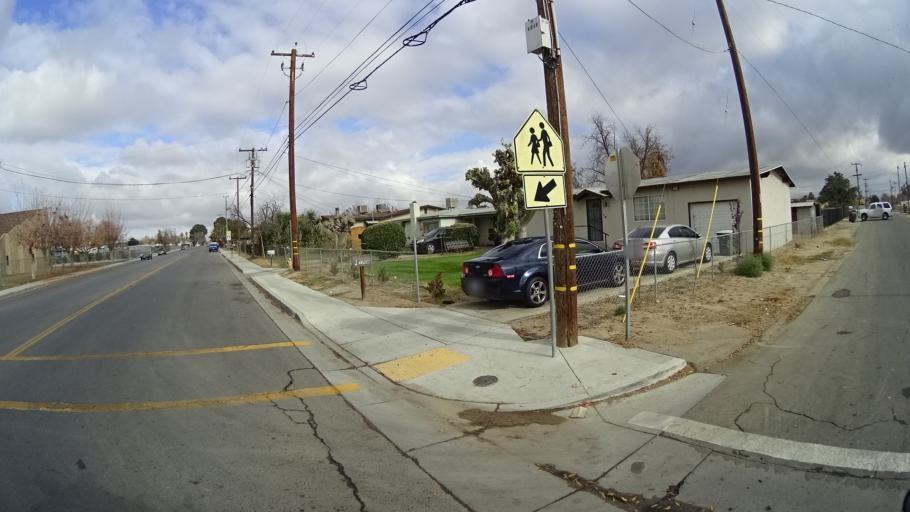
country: US
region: California
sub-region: Kern County
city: Bakersfield
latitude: 35.3367
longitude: -118.9942
